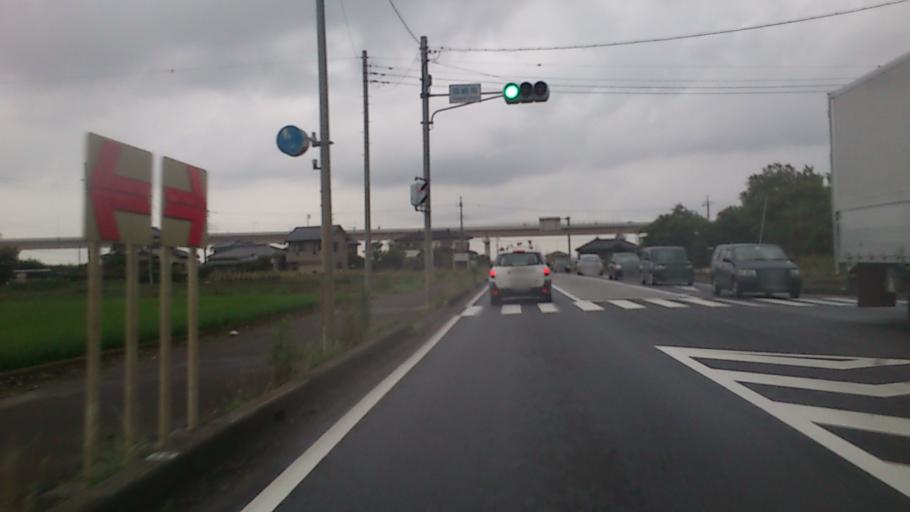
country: JP
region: Ibaraki
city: Sakai
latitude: 36.1177
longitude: 139.7750
